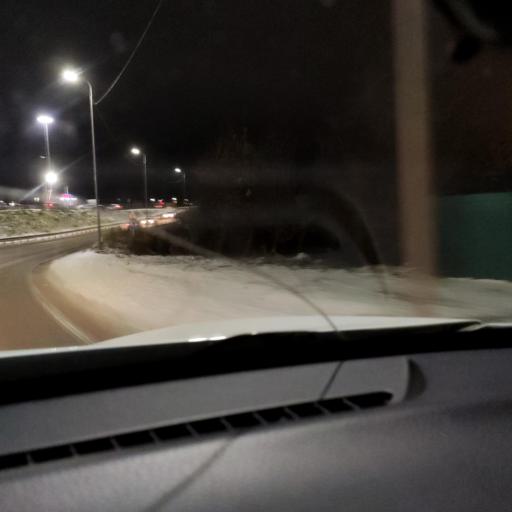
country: RU
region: Tatarstan
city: Osinovo
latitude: 55.8720
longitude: 48.8827
